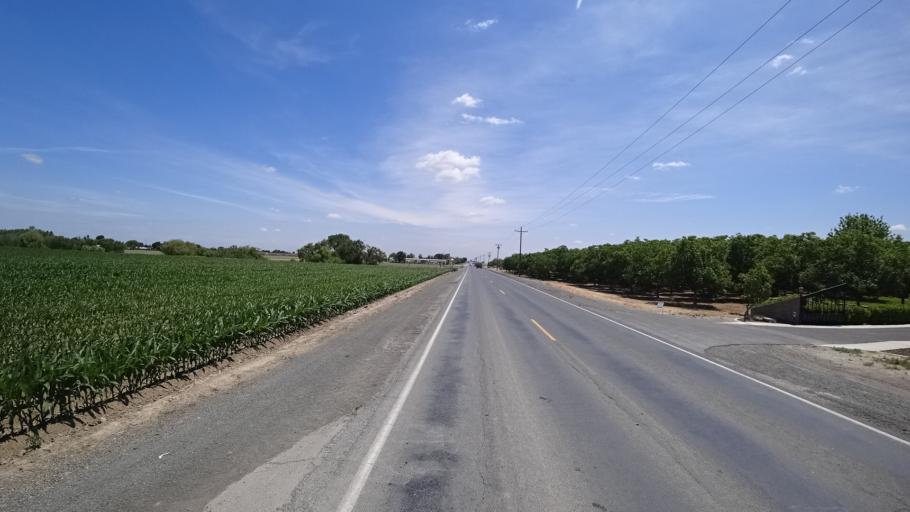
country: US
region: California
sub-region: Kings County
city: Home Garden
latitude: 36.2983
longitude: -119.6659
